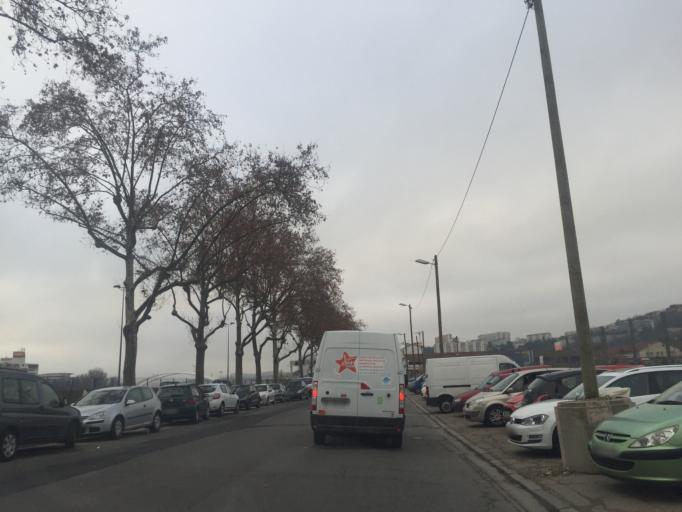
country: FR
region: Rhone-Alpes
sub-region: Departement du Rhone
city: La Mulatiere
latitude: 45.7394
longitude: 4.8224
